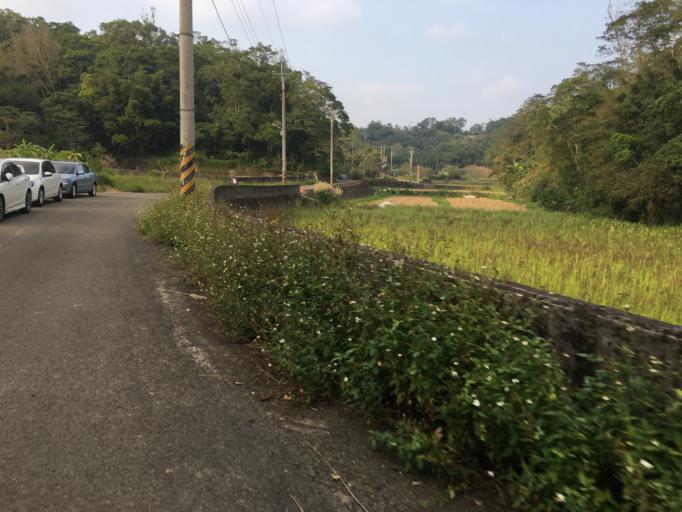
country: TW
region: Taiwan
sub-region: Hsinchu
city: Hsinchu
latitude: 24.7155
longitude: 121.0588
